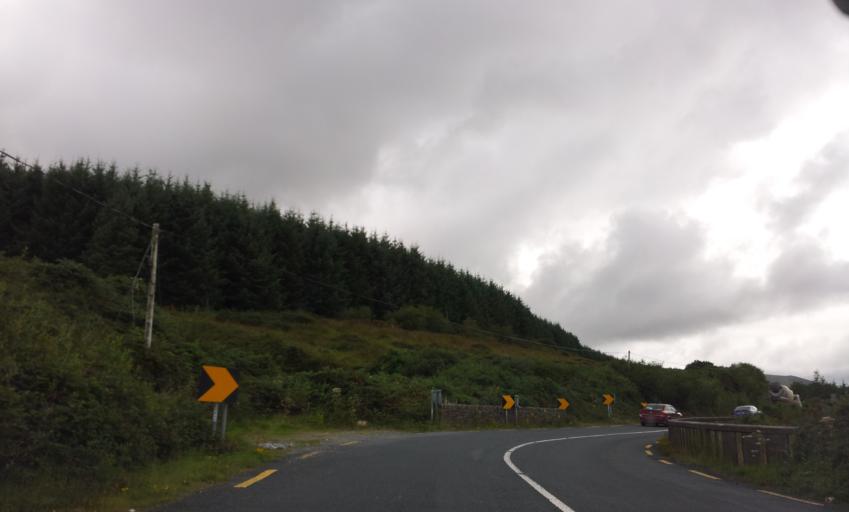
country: IE
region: Munster
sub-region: Ciarrai
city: Killorglin
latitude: 52.2177
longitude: -9.9251
